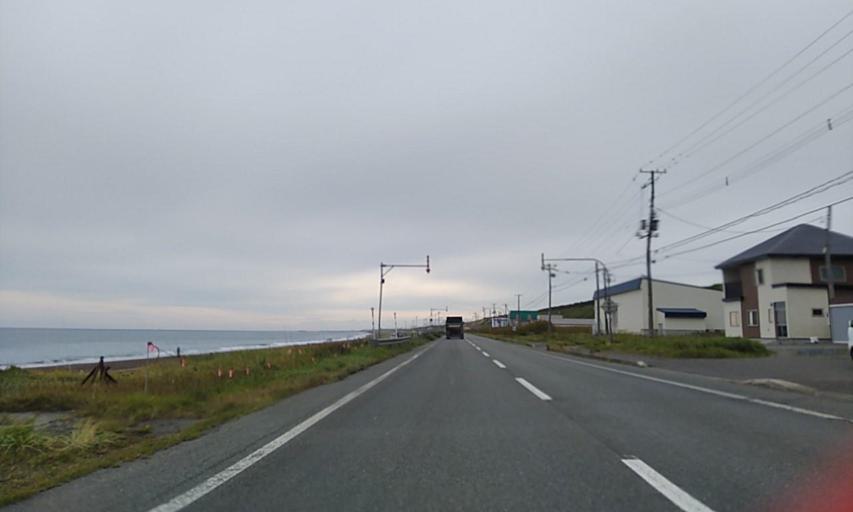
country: JP
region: Hokkaido
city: Makubetsu
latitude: 45.3757
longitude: 142.0981
